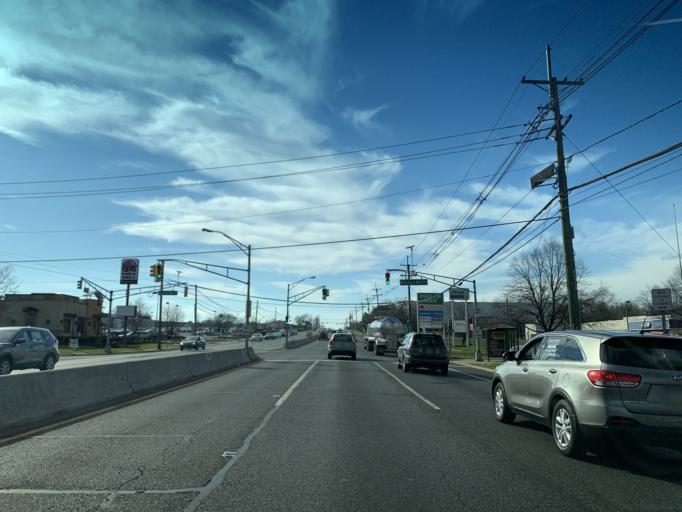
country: US
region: New Jersey
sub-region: Burlington County
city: Delanco
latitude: 40.0149
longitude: -74.9565
